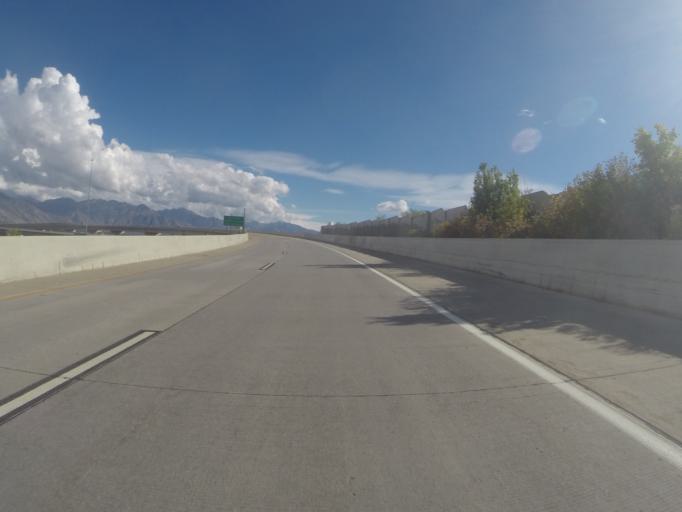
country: US
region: Utah
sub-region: Salt Lake County
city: Salt Lake City
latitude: 40.7585
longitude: -111.9150
